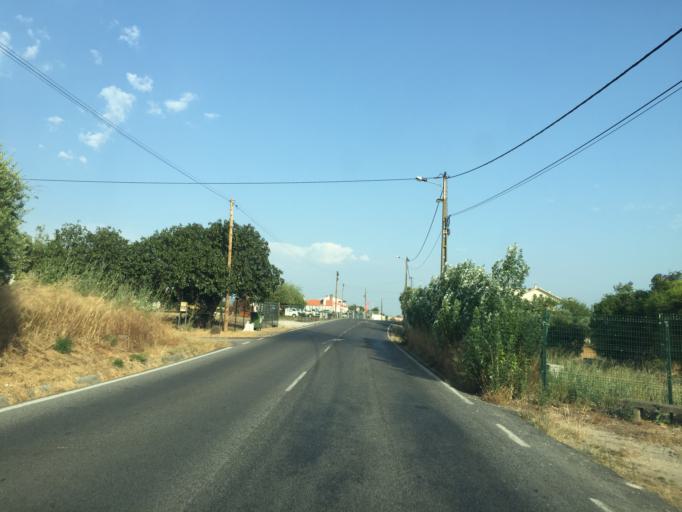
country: PT
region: Santarem
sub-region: Torres Novas
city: Torres Novas
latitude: 39.4791
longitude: -8.5710
